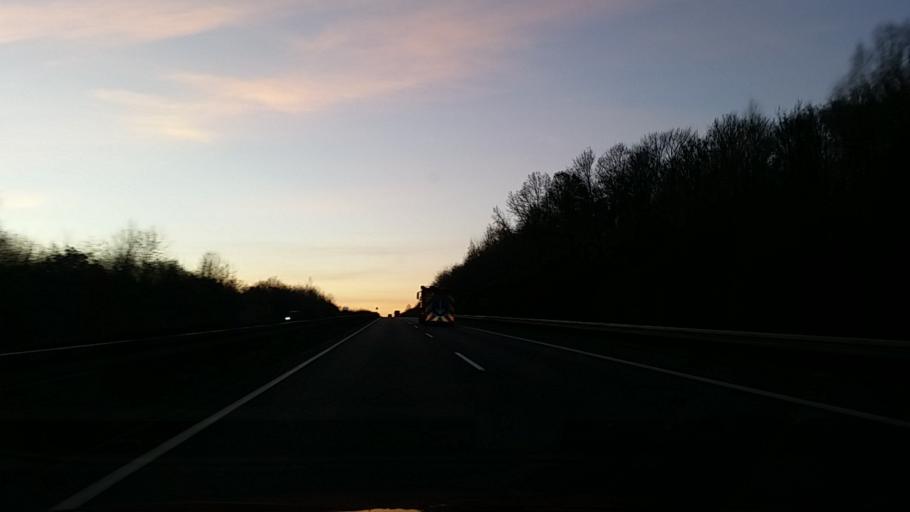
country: DE
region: Lower Saxony
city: Gielde
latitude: 52.0397
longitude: 10.5134
